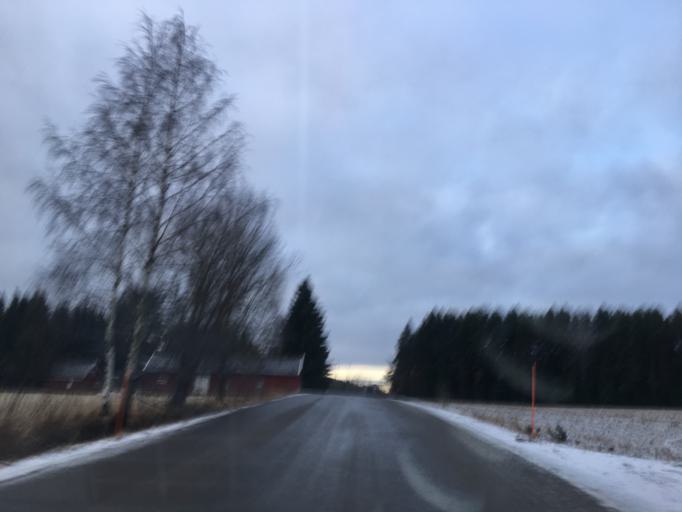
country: FI
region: Varsinais-Suomi
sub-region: Turku
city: Lieto
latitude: 60.5801
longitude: 22.5068
